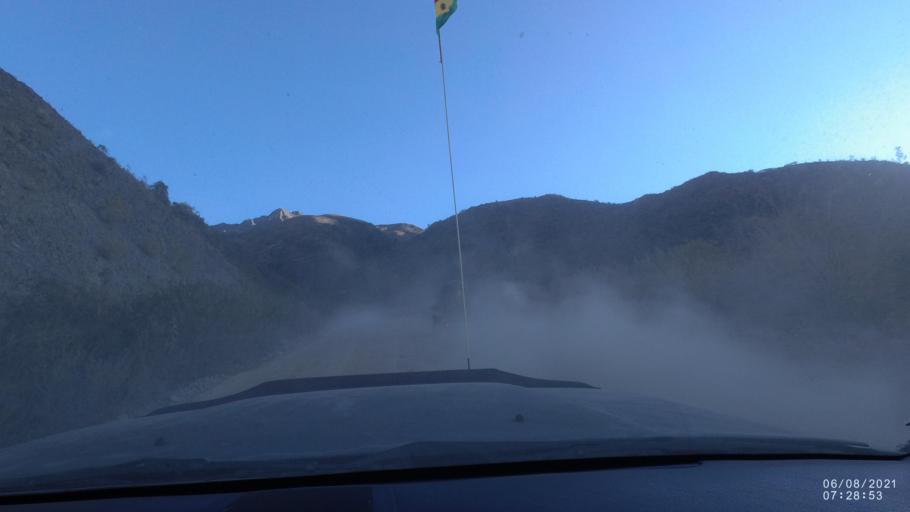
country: BO
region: Cochabamba
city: Sipe Sipe
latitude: -17.2806
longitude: -66.3187
